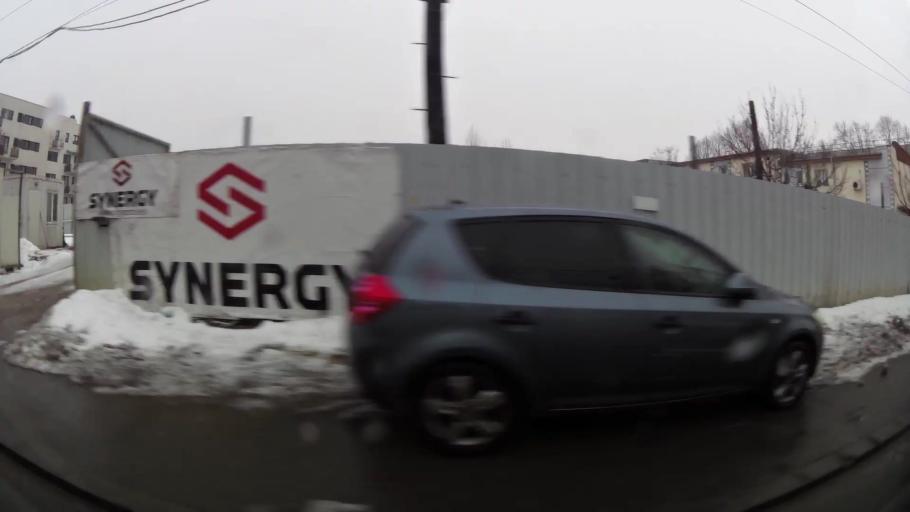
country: RO
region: Ilfov
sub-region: Comuna Otopeni
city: Otopeni
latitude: 44.4897
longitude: 26.0648
